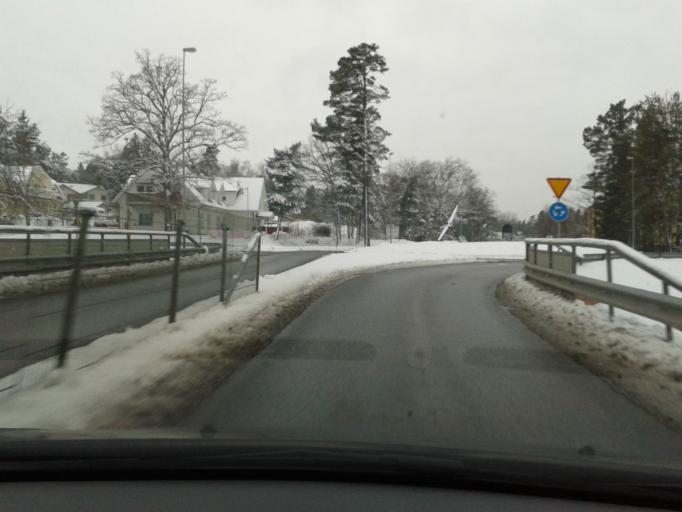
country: SE
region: Stockholm
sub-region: Nacka Kommun
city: Saltsjobaden
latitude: 59.2410
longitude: 18.2839
